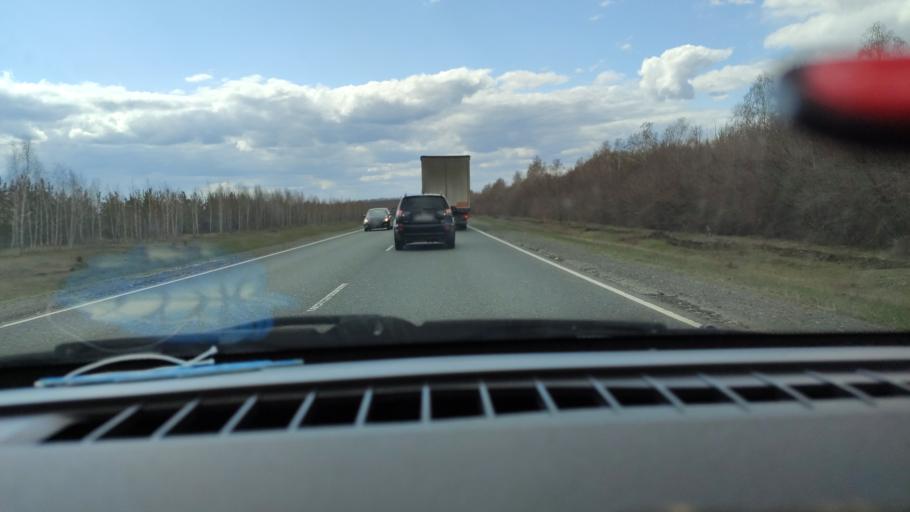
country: RU
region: Saratov
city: Balakovo
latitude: 52.1443
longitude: 47.8045
